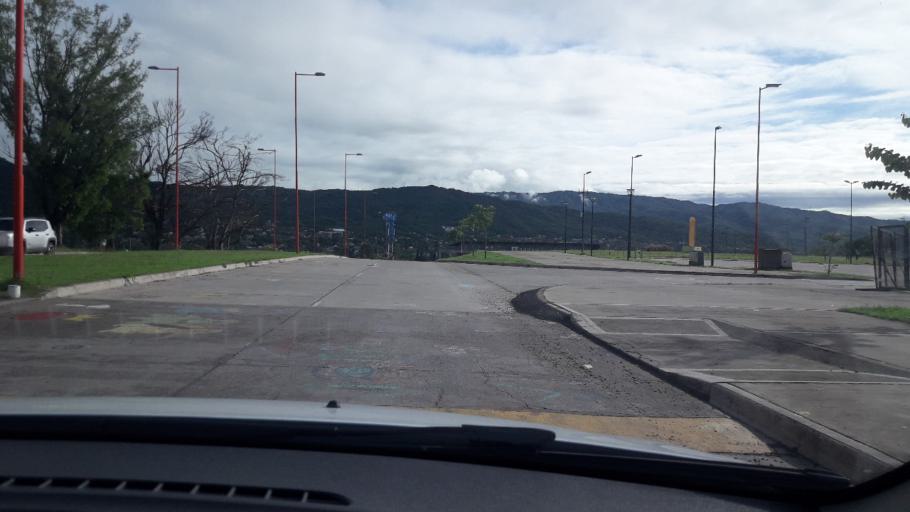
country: AR
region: Jujuy
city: San Salvador de Jujuy
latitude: -24.1813
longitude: -65.3299
